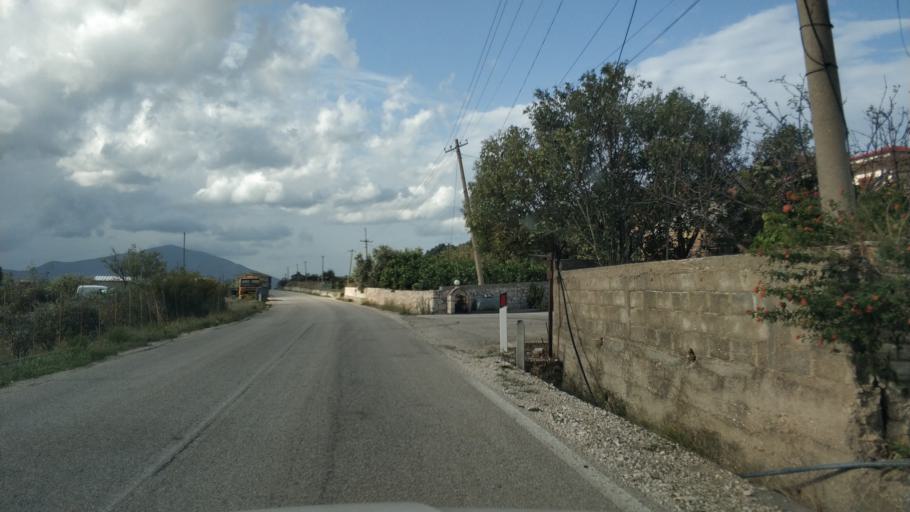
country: AL
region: Vlore
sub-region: Rrethi i Vlores
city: Orikum
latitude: 40.2965
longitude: 19.4895
